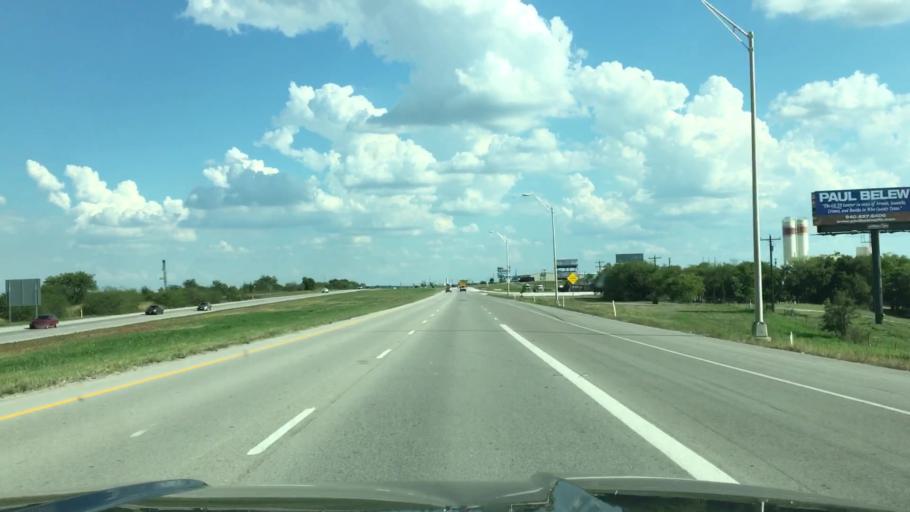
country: US
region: Texas
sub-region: Wise County
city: Decatur
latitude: 33.1941
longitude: -97.5597
